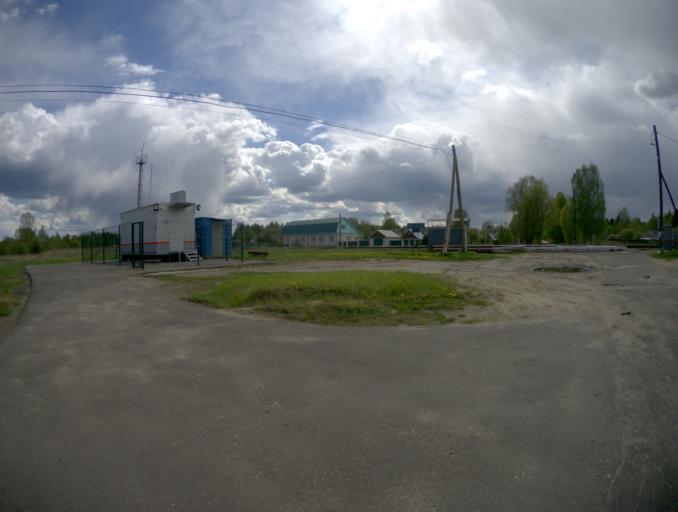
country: RU
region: Vladimir
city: Velikodvorskiy
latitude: 55.2407
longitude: 40.6564
